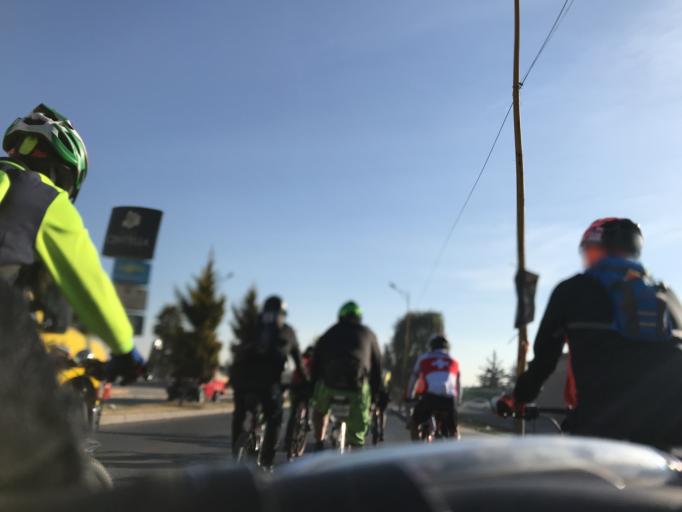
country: MX
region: Mexico
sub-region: Tultepec
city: Tultepec
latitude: 19.6780
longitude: -99.1489
